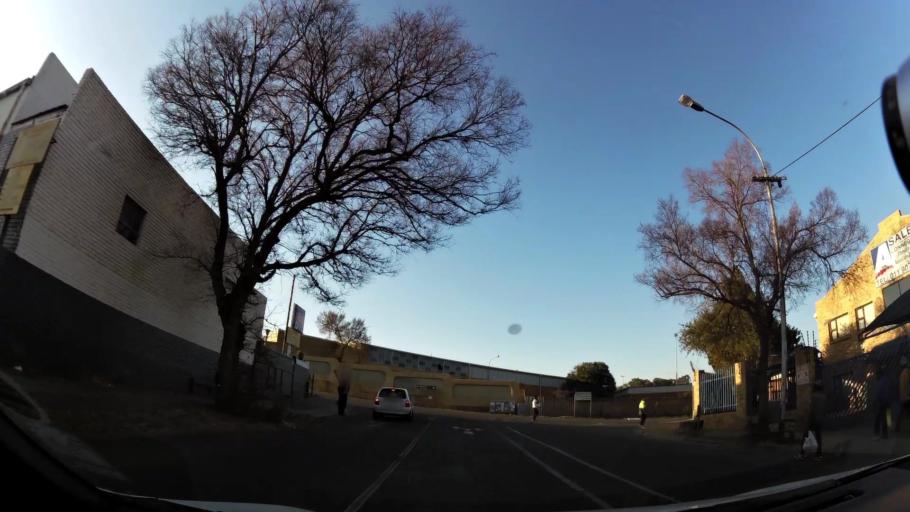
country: ZA
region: Gauteng
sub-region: Ekurhuleni Metropolitan Municipality
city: Germiston
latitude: -26.2530
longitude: 28.1321
